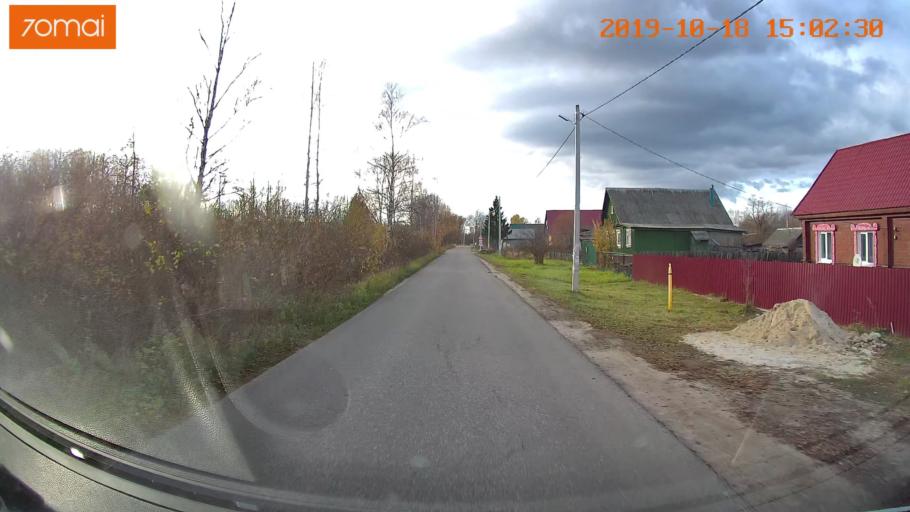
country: RU
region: Vladimir
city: Gus'-Khrustal'nyy
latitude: 55.5030
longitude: 40.6060
